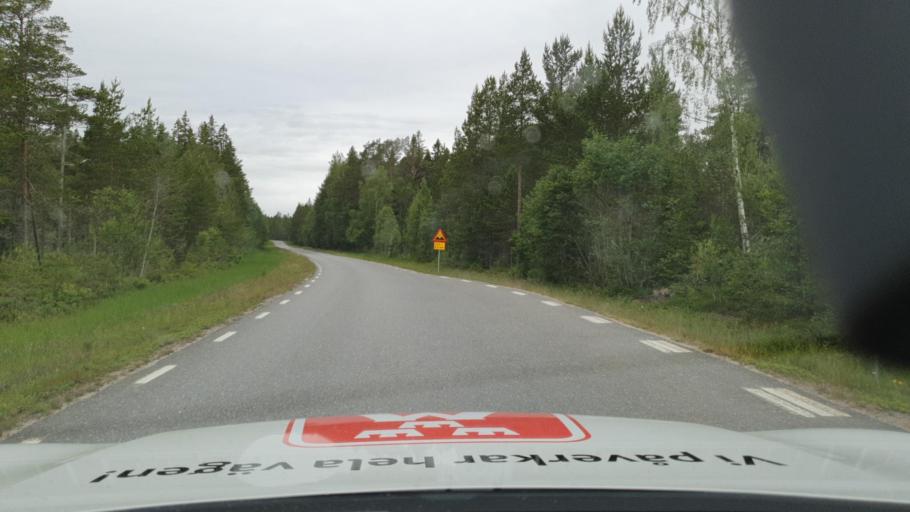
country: SE
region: Vaesterbotten
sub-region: Nordmalings Kommun
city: Nordmaling
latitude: 63.4329
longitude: 19.4849
